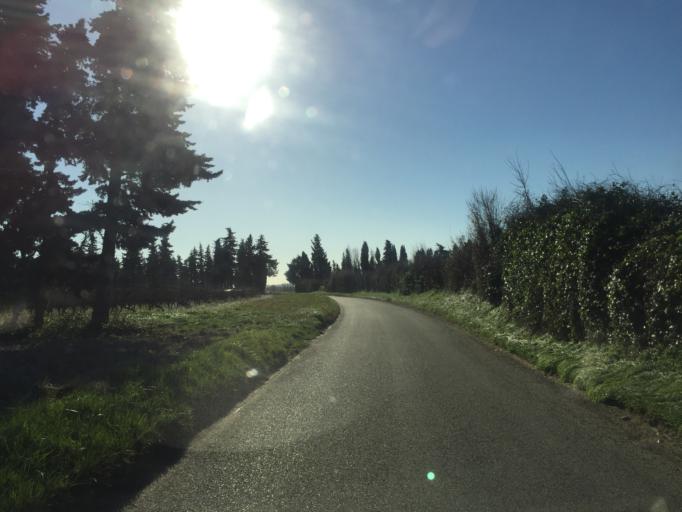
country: FR
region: Provence-Alpes-Cote d'Azur
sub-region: Departement du Vaucluse
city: Courthezon
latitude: 44.0763
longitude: 4.9060
